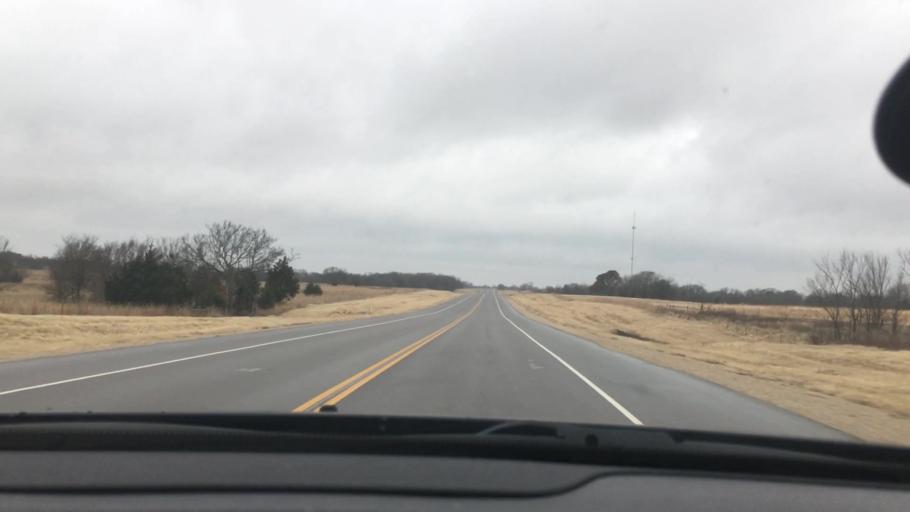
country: US
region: Oklahoma
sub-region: Johnston County
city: Tishomingo
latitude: 34.3267
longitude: -96.6608
